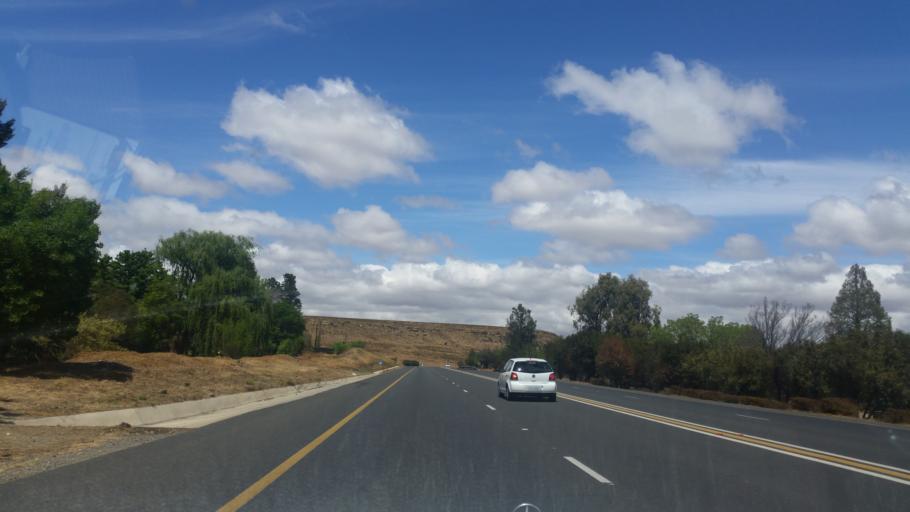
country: ZA
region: Orange Free State
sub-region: Thabo Mofutsanyana District Municipality
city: Harrismith
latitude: -28.2790
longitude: 29.1406
